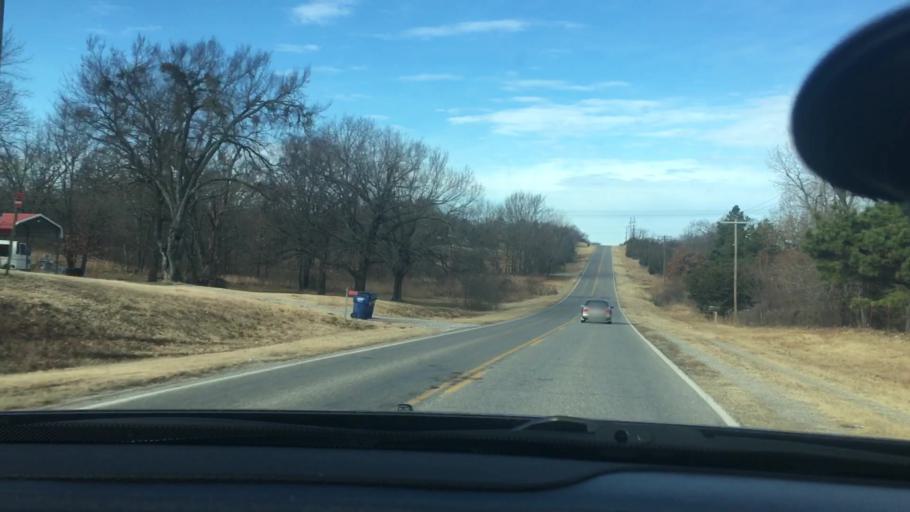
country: US
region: Oklahoma
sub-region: Seminole County
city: Konawa
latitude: 34.9462
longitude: -96.7293
